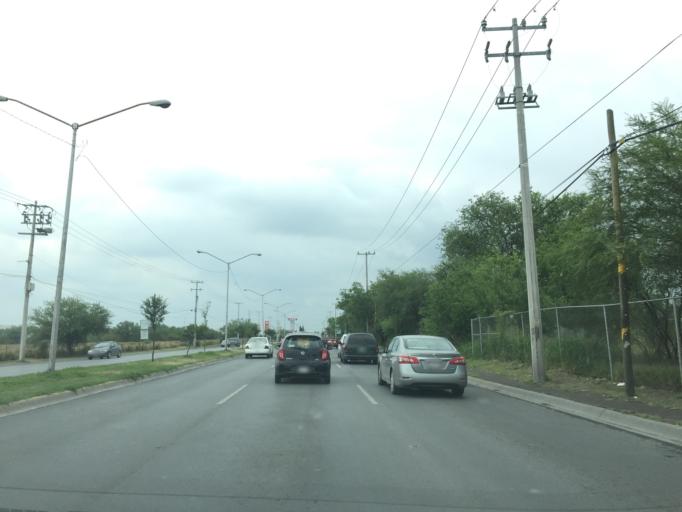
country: MX
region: Nuevo Leon
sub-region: Apodaca
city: Fraccionamiento Cosmopolis Octavo Sector
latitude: 25.7840
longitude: -100.2319
